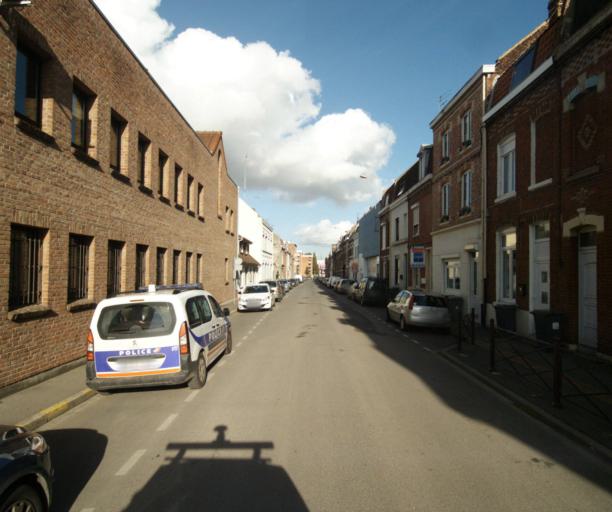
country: FR
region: Nord-Pas-de-Calais
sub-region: Departement du Nord
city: Armentieres
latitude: 50.6874
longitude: 2.8861
